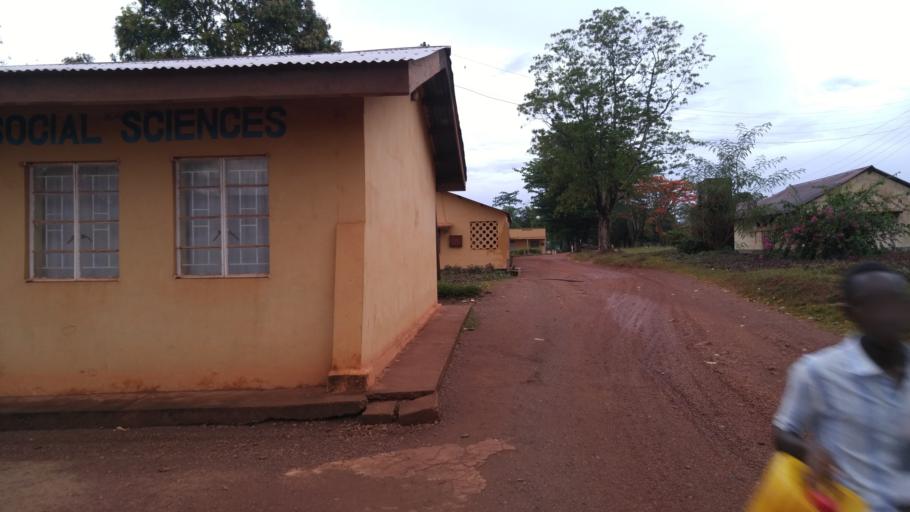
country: SL
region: Southern Province
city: Largo
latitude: 8.1135
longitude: -12.0711
